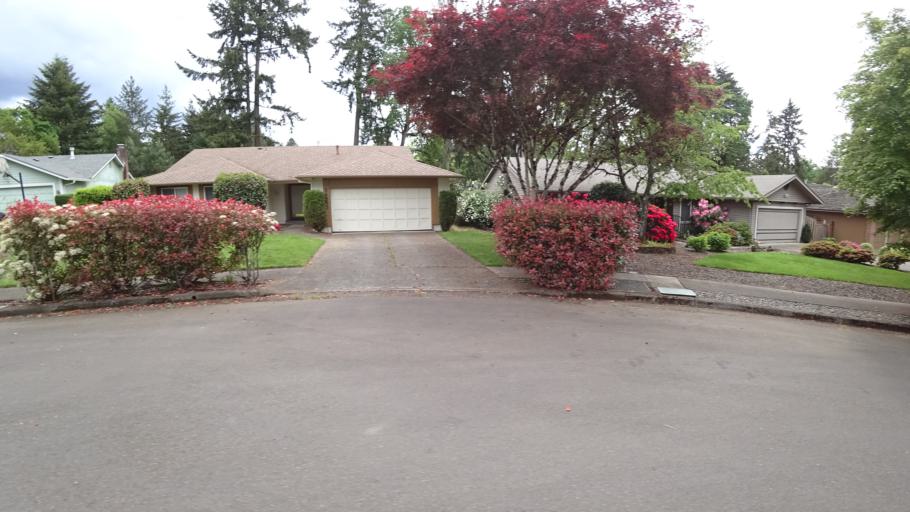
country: US
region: Oregon
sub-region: Washington County
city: Beaverton
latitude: 45.4784
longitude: -122.8268
